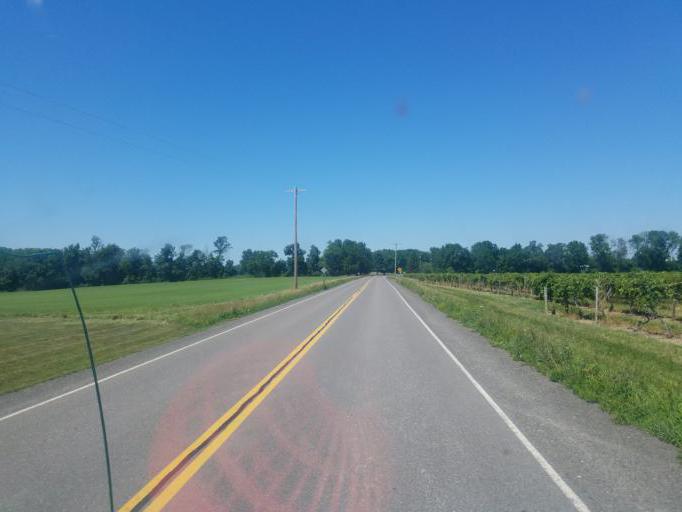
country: US
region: New York
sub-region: Yates County
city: Penn Yan
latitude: 42.7060
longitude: -76.9989
